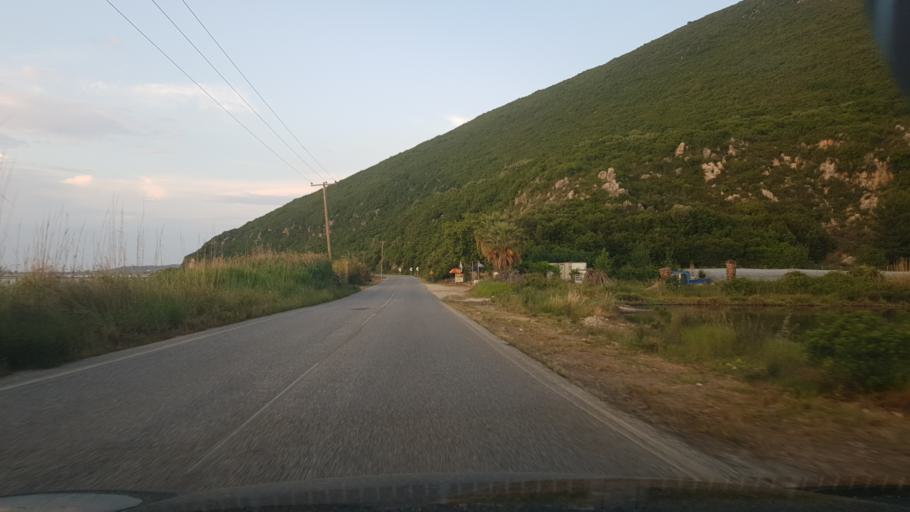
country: GR
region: Ionian Islands
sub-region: Lefkada
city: Lefkada
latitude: 38.8499
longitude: 20.7425
